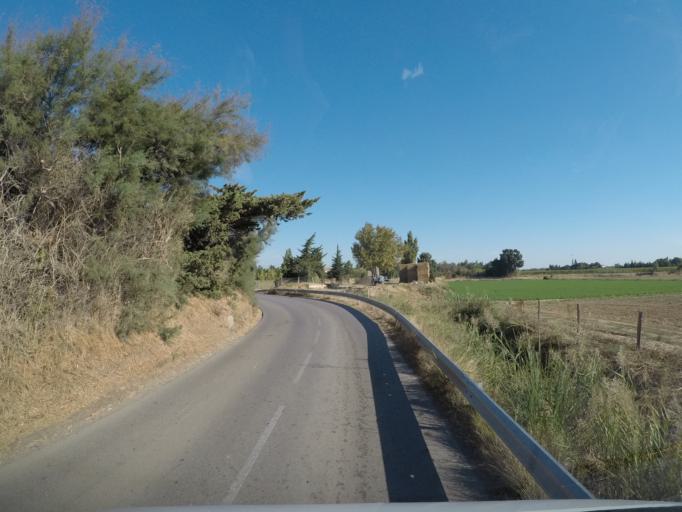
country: FR
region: Languedoc-Roussillon
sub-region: Departement de l'Aude
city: Narbonne
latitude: 43.1635
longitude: 3.0112
